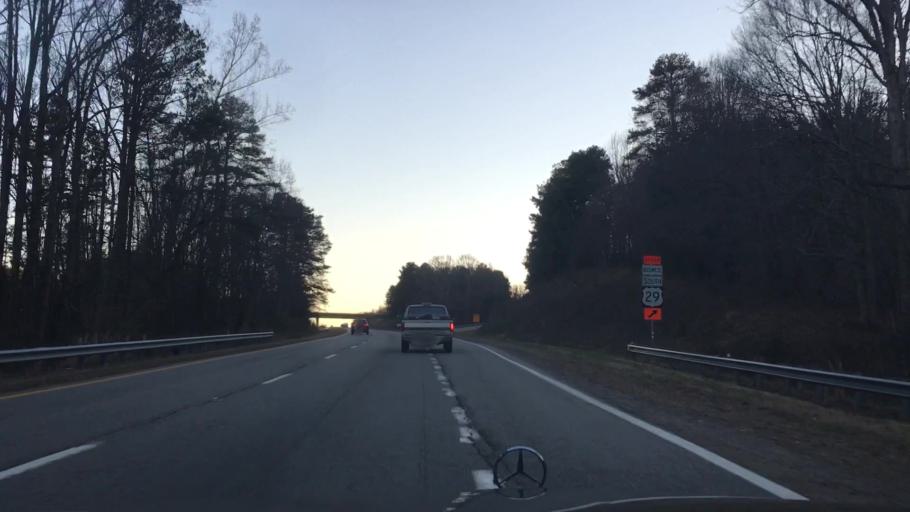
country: US
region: Virginia
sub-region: Pittsylvania County
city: Hurt
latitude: 37.1187
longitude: -79.3242
